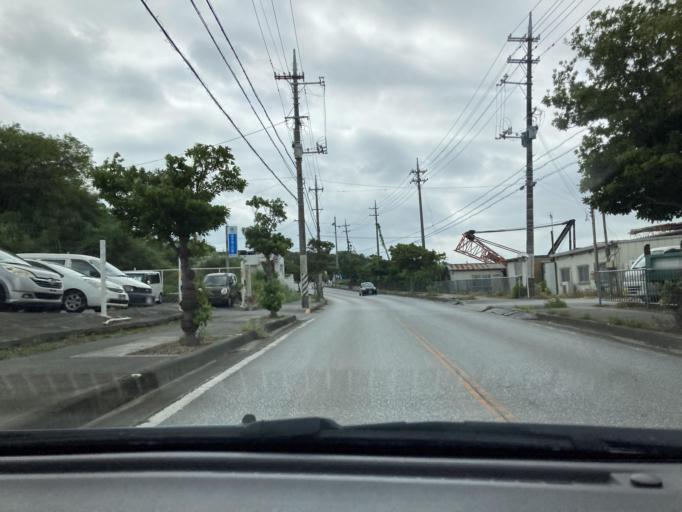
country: JP
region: Okinawa
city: Ginowan
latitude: 26.2605
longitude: 127.7768
